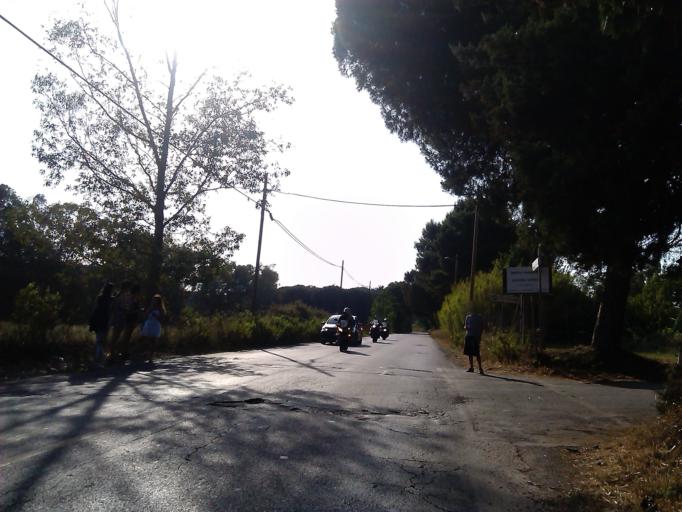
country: IT
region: Latium
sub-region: Citta metropolitana di Roma Capitale
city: Rome
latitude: 41.8257
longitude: 12.5263
